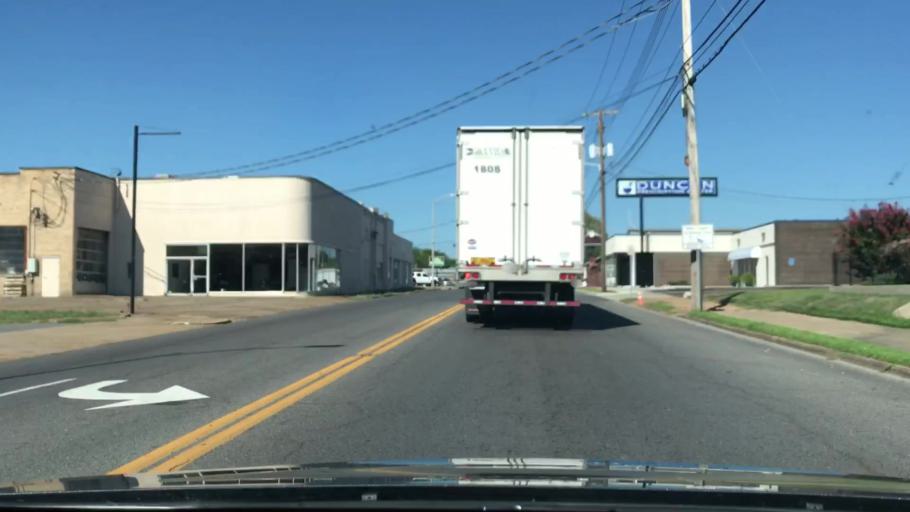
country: US
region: Kentucky
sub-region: Graves County
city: Mayfield
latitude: 36.7417
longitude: -88.6389
